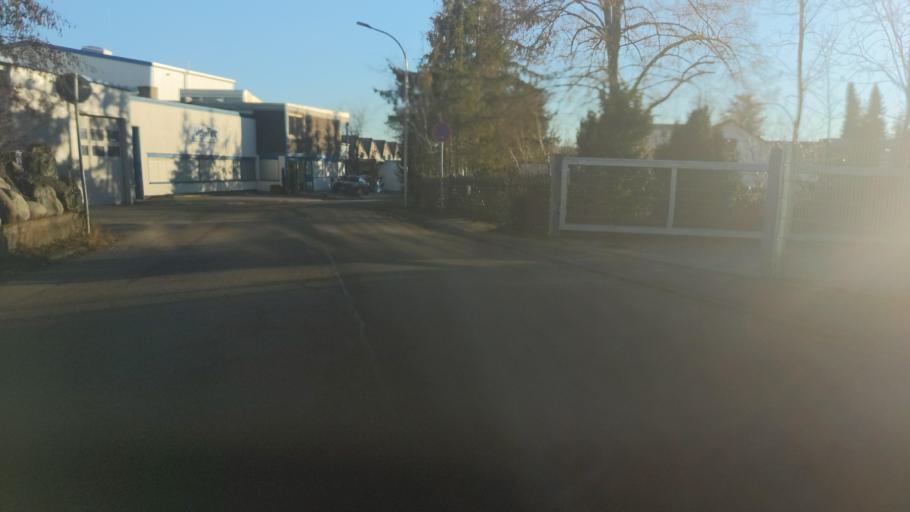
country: DE
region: Baden-Wuerttemberg
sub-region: Regierungsbezirk Stuttgart
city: Renningen
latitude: 48.7765
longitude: 8.9293
